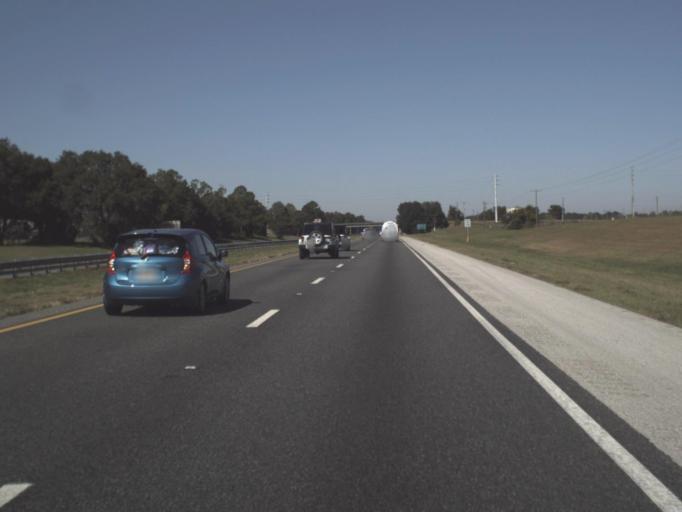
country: US
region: Florida
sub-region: Sumter County
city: Wildwood
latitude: 28.7957
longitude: -81.9947
